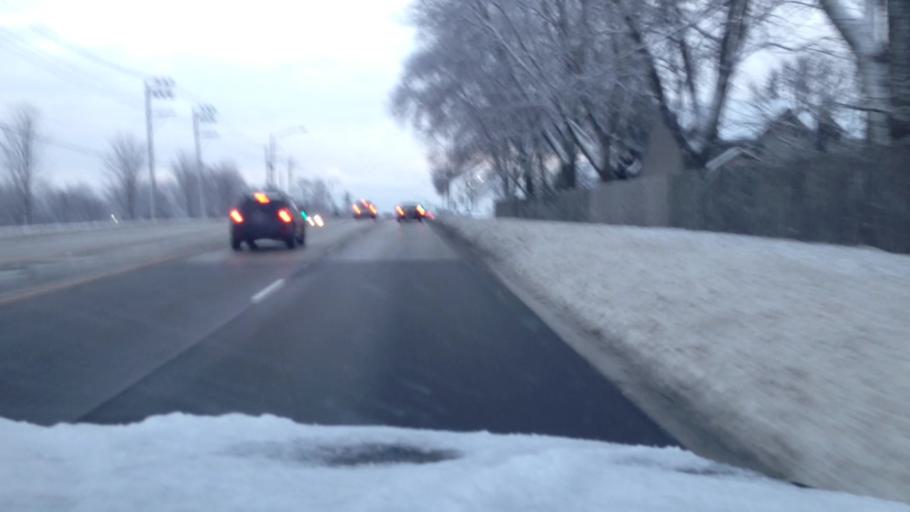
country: US
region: Illinois
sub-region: Kane County
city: South Elgin
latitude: 42.0089
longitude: -88.3151
